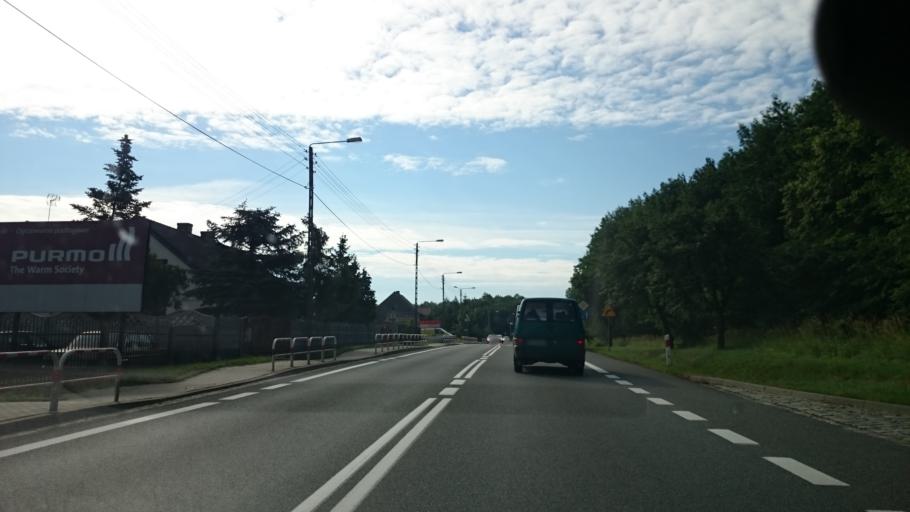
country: PL
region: Opole Voivodeship
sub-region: Powiat opolski
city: Tarnow Opolski
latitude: 50.6008
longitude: 18.0834
